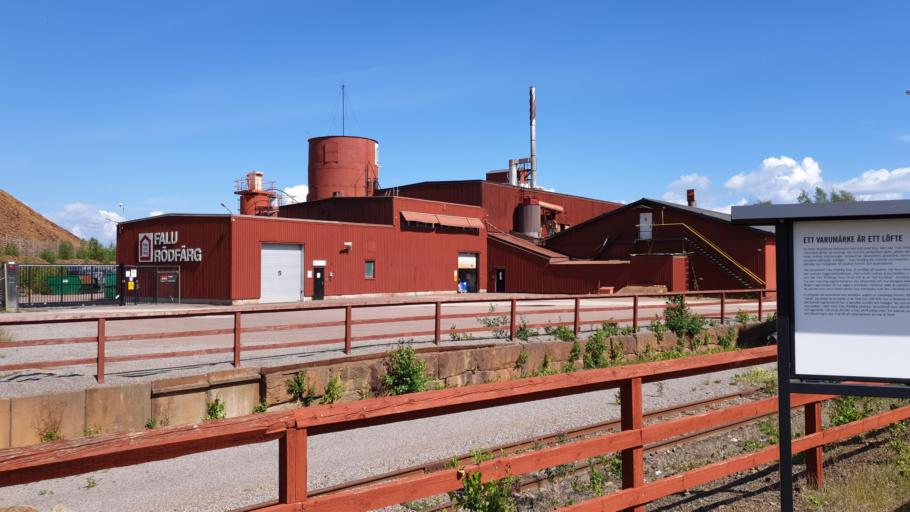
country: SE
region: Dalarna
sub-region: Faluns Kommun
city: Falun
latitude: 60.5991
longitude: 15.6170
